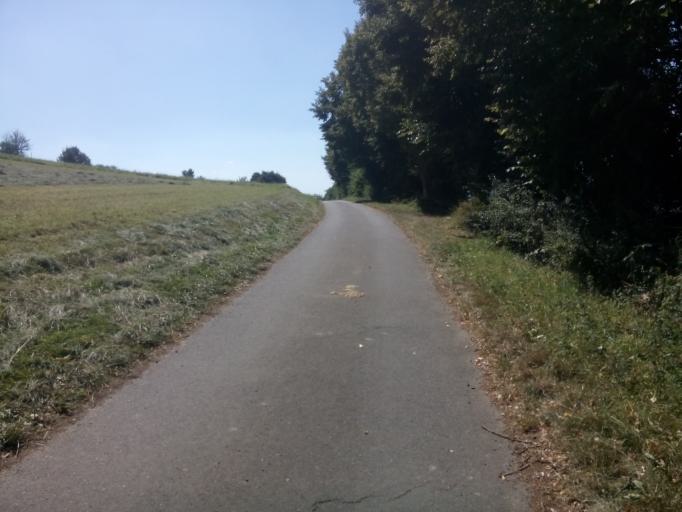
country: DE
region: Hesse
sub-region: Regierungsbezirk Darmstadt
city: Brensbach
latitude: 49.8210
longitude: 8.9091
